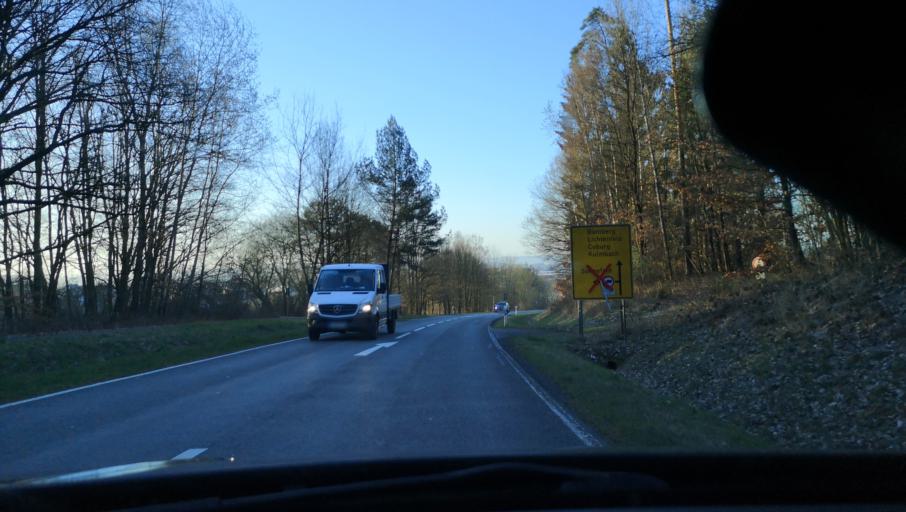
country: DE
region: Bavaria
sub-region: Upper Franconia
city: Sonnefeld
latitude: 50.2305
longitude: 11.1250
